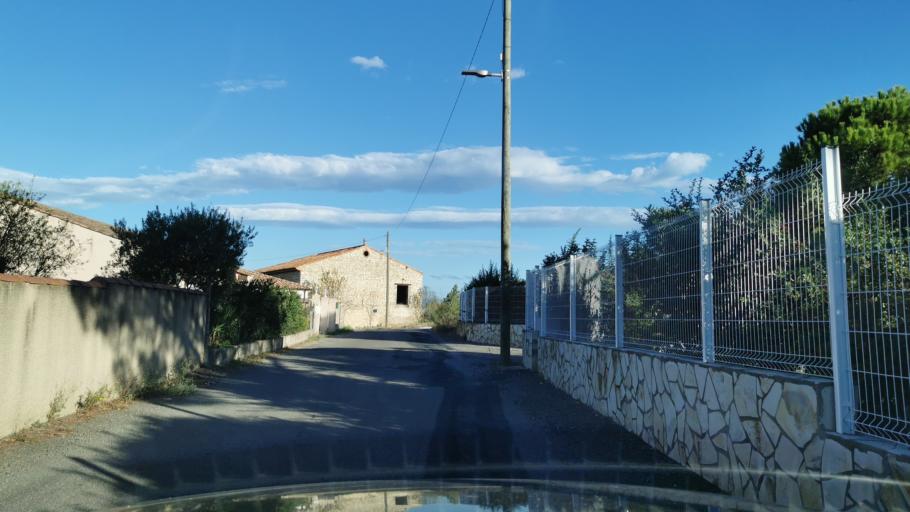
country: FR
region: Languedoc-Roussillon
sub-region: Departement de l'Aude
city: Ouveillan
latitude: 43.2658
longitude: 2.9968
